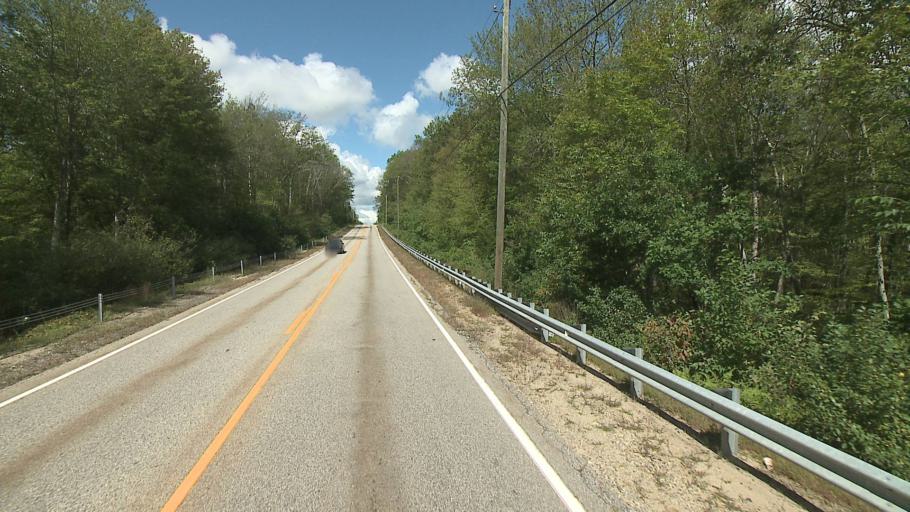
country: US
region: Connecticut
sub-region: Windham County
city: South Woodstock
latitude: 41.8639
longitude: -72.0455
